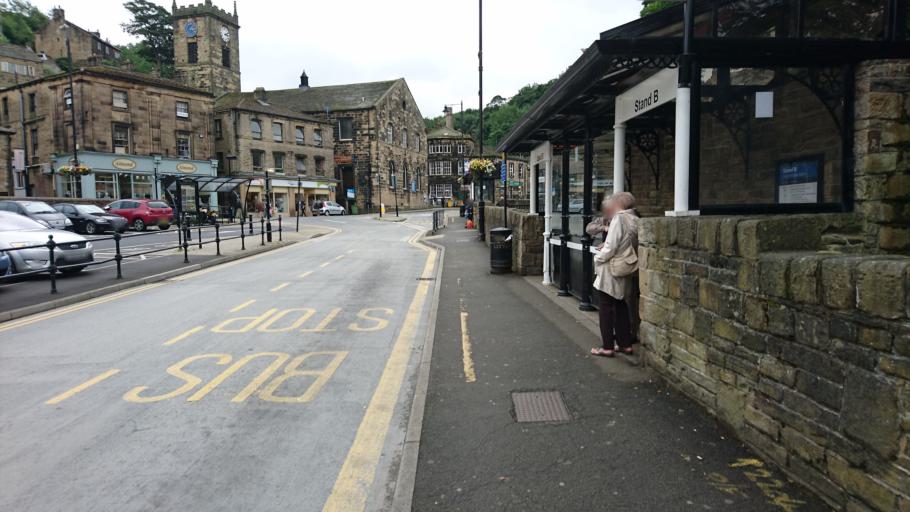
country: GB
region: England
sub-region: Kirklees
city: Holmfirth
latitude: 53.5707
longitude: -1.7864
